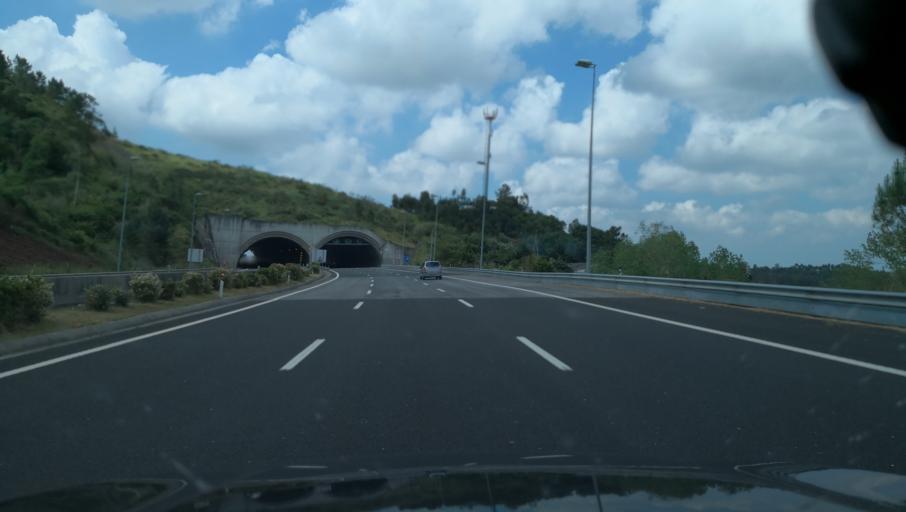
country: PT
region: Leiria
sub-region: Caldas da Rainha
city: Caldas da Rainha
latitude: 39.4633
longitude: -9.1167
